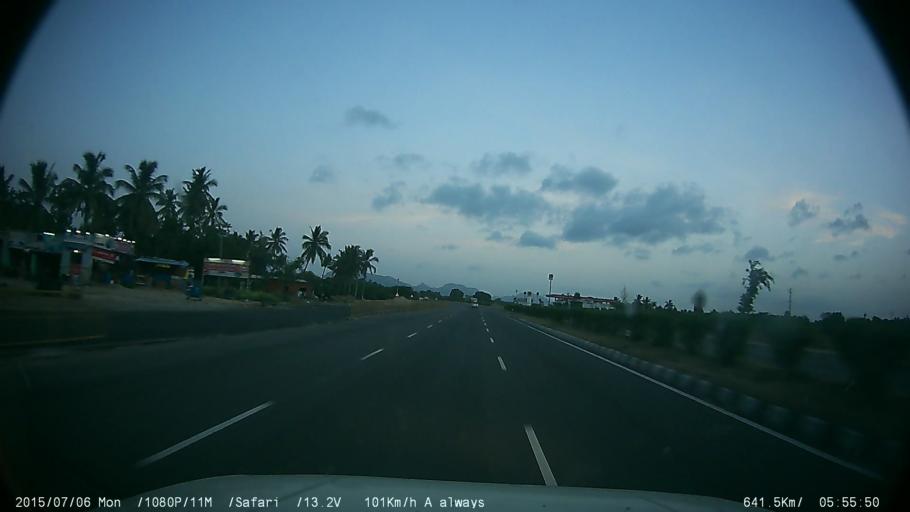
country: IN
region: Tamil Nadu
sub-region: Krishnagiri
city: Krishnagiri
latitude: 12.5675
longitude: 78.1753
